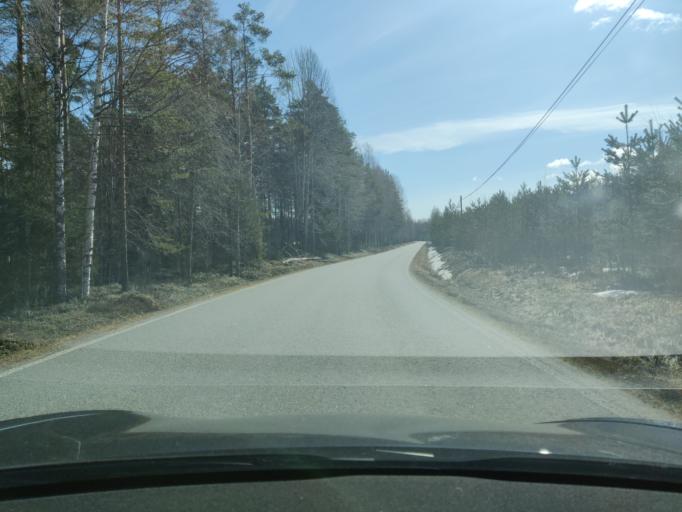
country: FI
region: Northern Savo
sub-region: Kuopio
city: Vehmersalmi
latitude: 62.7712
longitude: 27.9809
